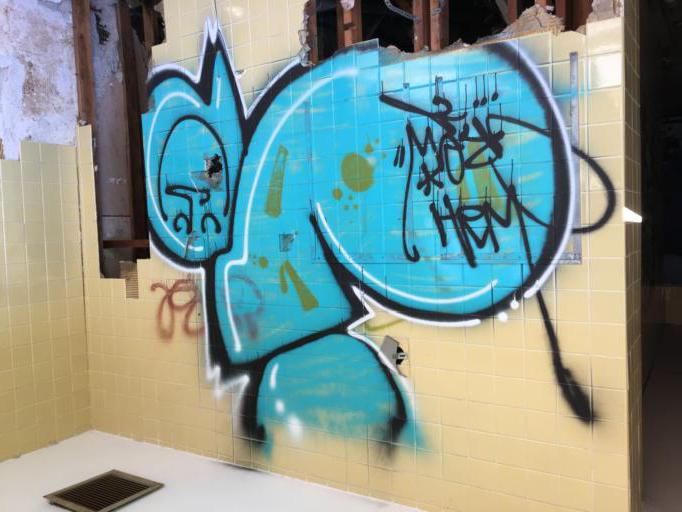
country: US
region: Michigan
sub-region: Wayne County
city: Dearborn
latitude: 42.3435
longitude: -83.1198
